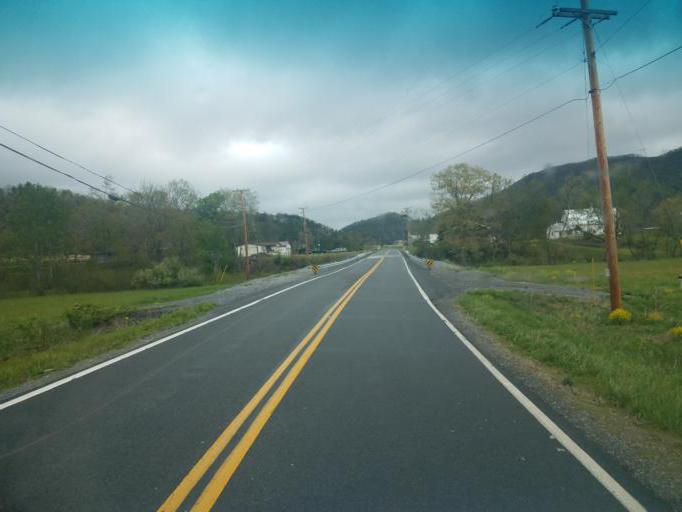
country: US
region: Virginia
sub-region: Bland County
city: Bland
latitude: 37.1746
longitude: -81.1468
